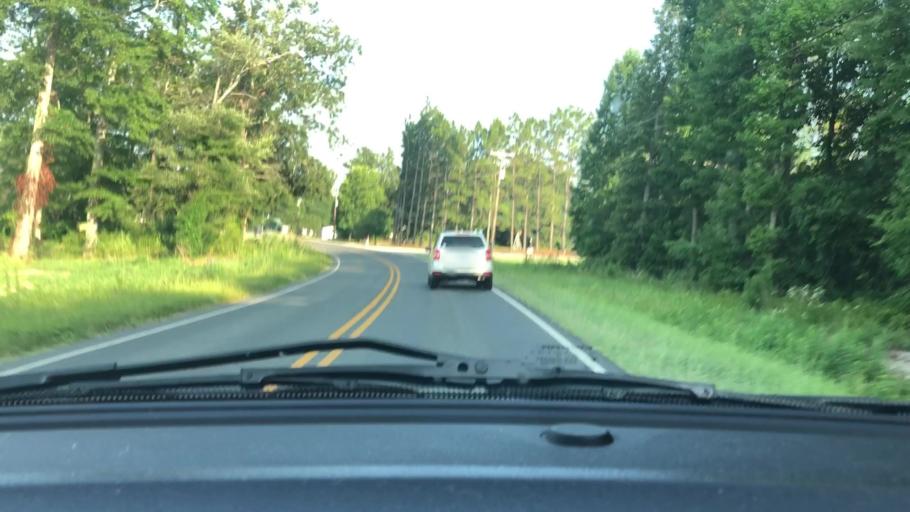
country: US
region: North Carolina
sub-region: Lee County
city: Broadway
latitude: 35.3483
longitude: -79.0700
